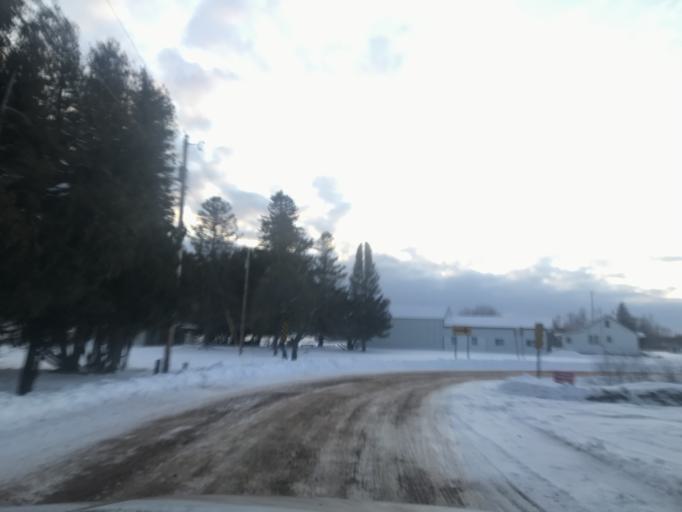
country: US
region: Michigan
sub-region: Menominee County
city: Menominee
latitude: 45.4122
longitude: -87.3450
